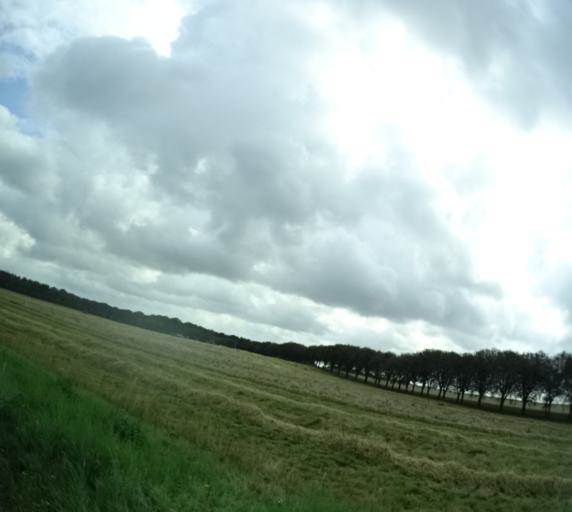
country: DK
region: Central Jutland
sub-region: Syddjurs Kommune
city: Ryomgard
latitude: 56.3916
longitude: 10.5118
